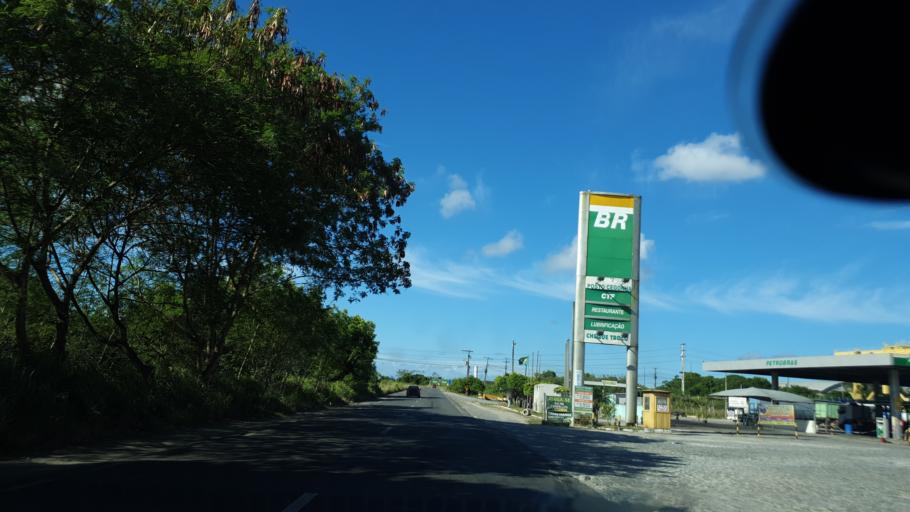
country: BR
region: Bahia
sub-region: Camacari
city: Camacari
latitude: -12.6742
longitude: -38.3004
